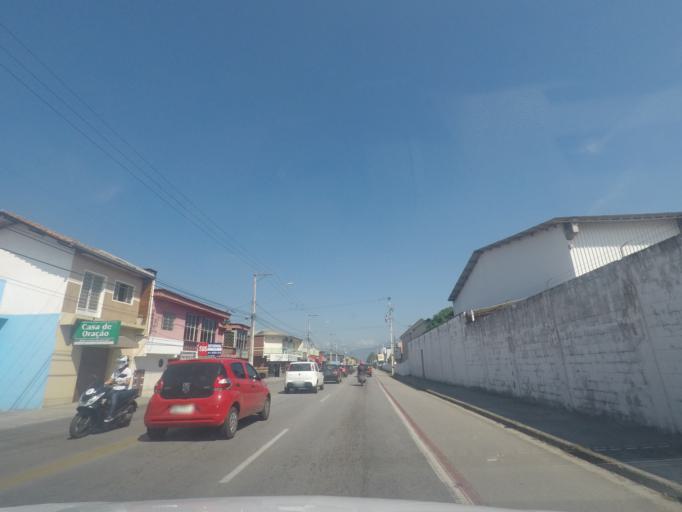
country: BR
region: Parana
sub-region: Paranagua
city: Paranagua
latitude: -25.5459
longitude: -48.5419
